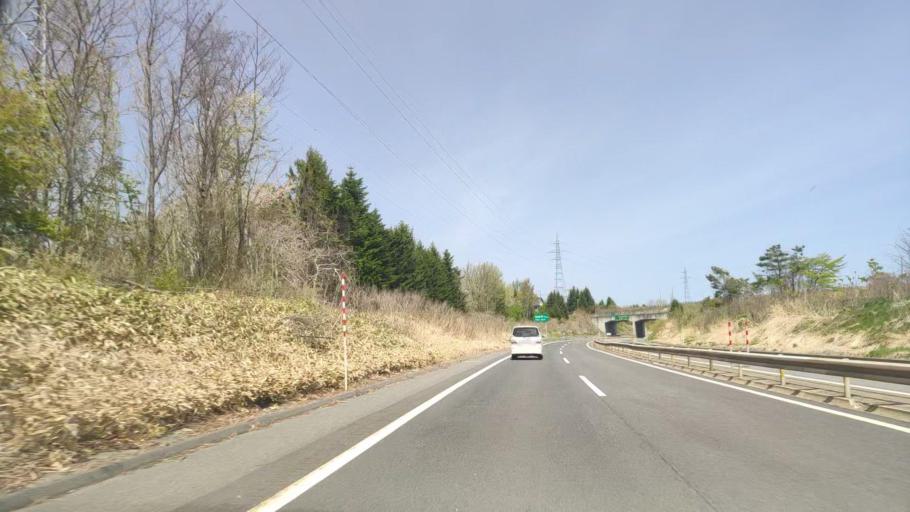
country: JP
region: Aomori
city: Hachinohe
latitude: 40.4759
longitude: 141.4599
